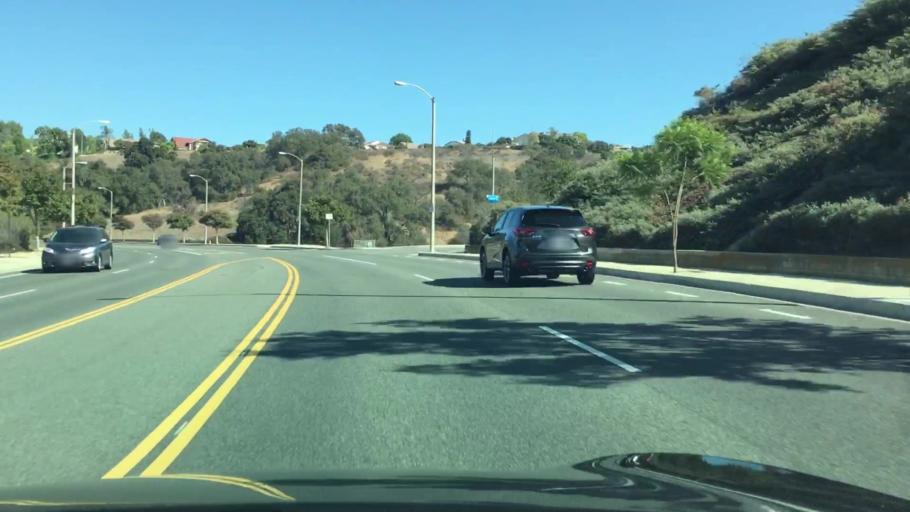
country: US
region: California
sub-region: Los Angeles County
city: Rowland Heights
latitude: 33.9714
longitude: -117.8677
